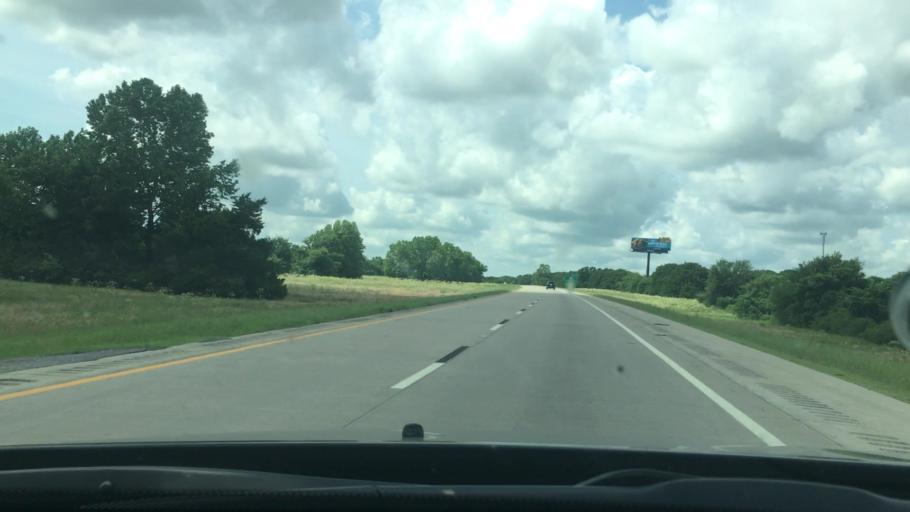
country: US
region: Oklahoma
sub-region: Love County
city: Marietta
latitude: 33.8157
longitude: -97.1329
